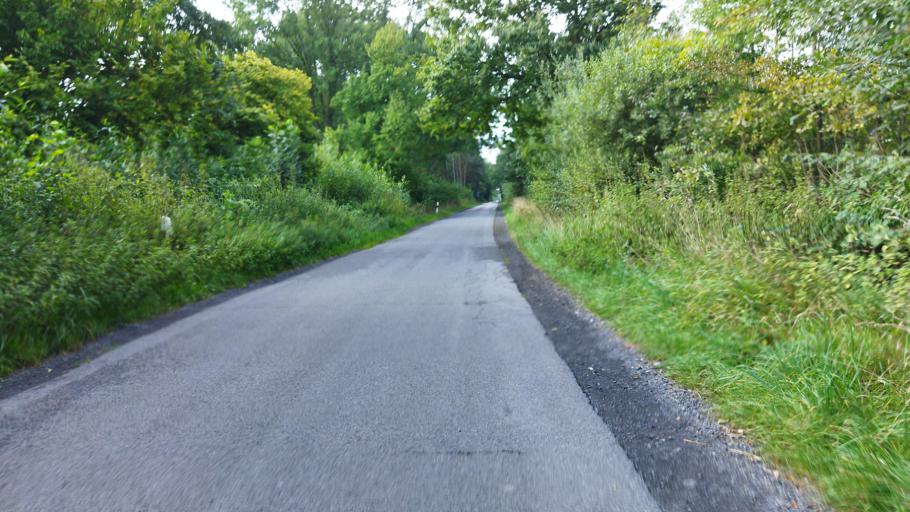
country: DE
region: North Rhine-Westphalia
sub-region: Regierungsbezirk Munster
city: Sassenberg
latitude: 52.0099
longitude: 8.0578
